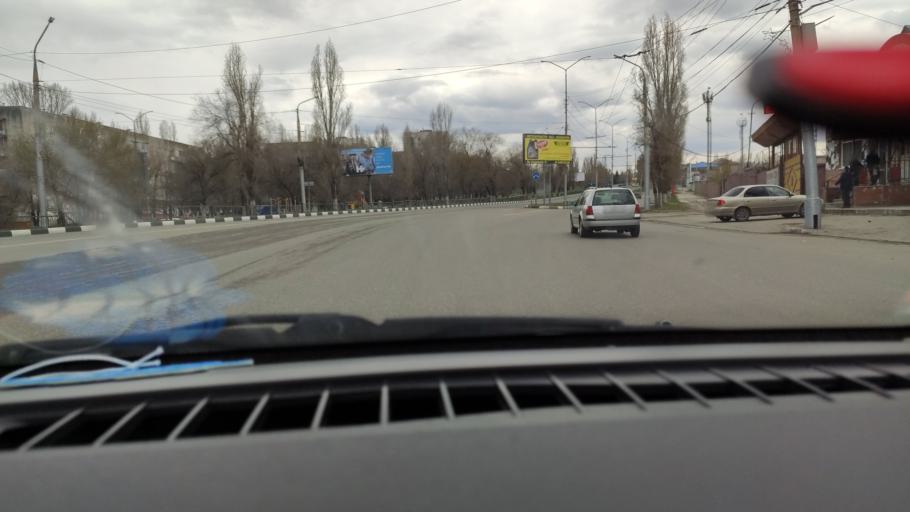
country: RU
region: Saratov
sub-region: Saratovskiy Rayon
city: Saratov
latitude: 51.6111
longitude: 45.9696
